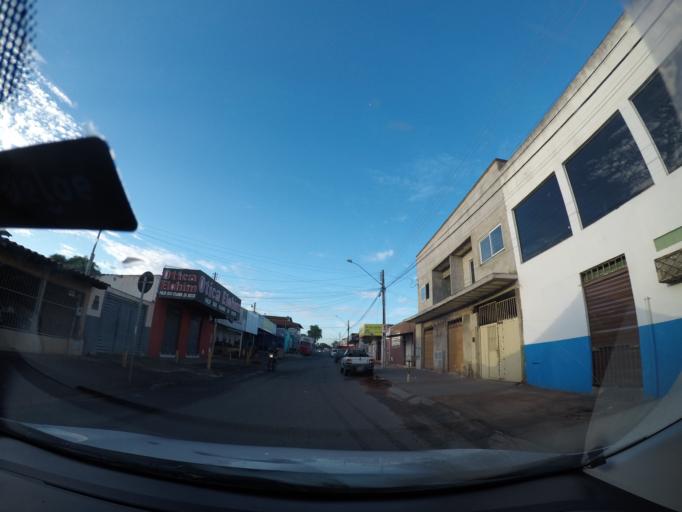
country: BR
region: Goias
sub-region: Goiania
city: Goiania
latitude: -16.6986
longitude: -49.3520
